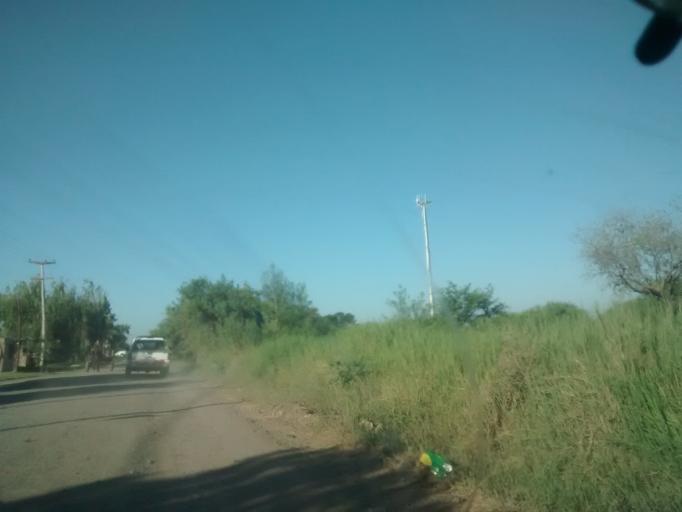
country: AR
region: Chaco
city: Resistencia
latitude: -27.4597
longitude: -59.0247
